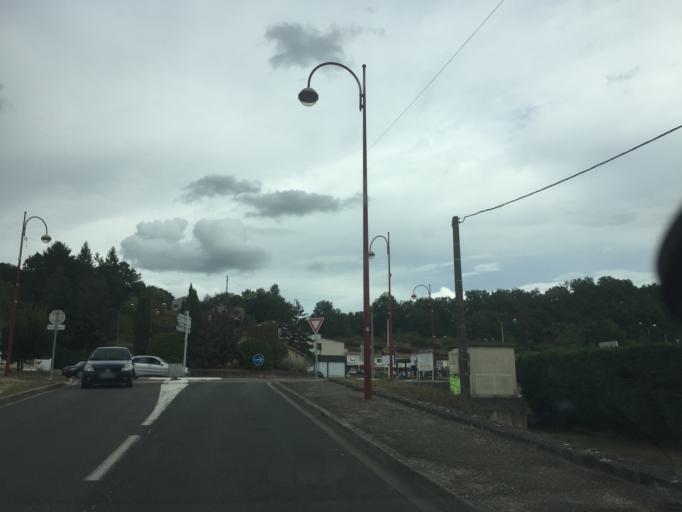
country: FR
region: Aquitaine
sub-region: Departement du Lot-et-Garonne
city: Monsempron-Libos
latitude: 44.4932
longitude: 0.9473
